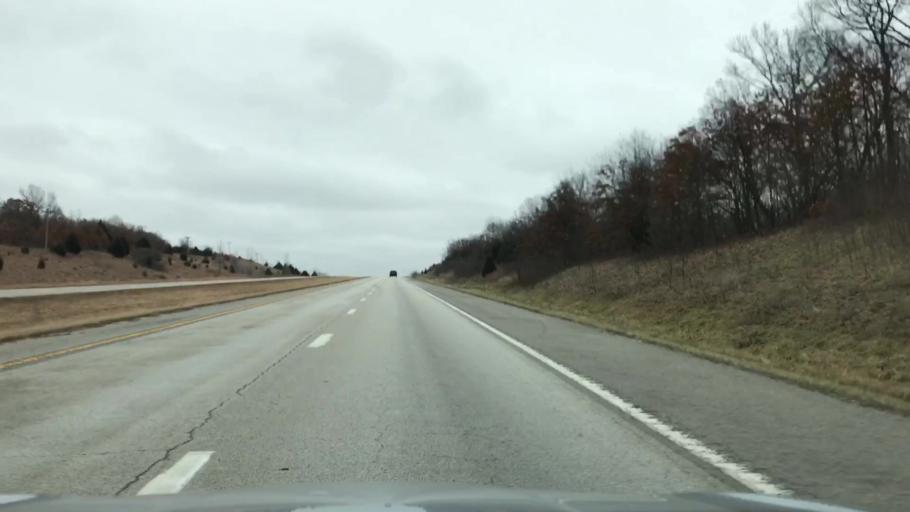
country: US
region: Missouri
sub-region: Clinton County
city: Cameron
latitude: 39.7512
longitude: -94.1558
